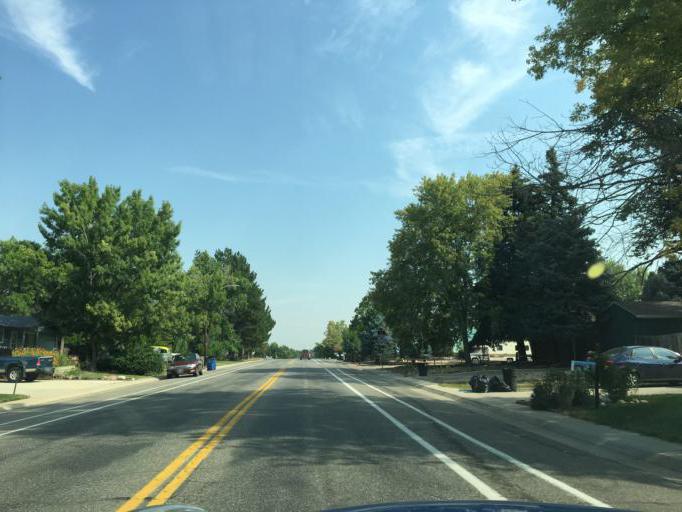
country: US
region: Colorado
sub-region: Jefferson County
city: Arvada
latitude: 39.8151
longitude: -105.0673
